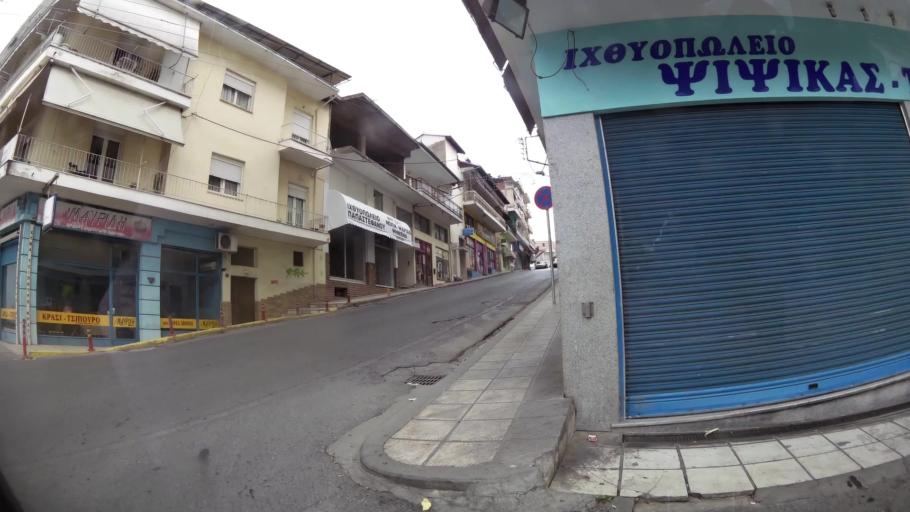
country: GR
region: Central Macedonia
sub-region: Nomos Imathias
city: Veroia
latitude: 40.5247
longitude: 22.2014
